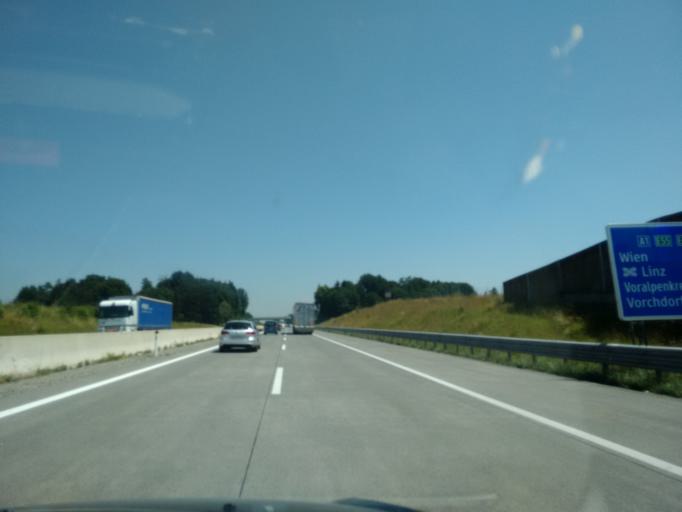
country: AT
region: Upper Austria
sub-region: Politischer Bezirk Gmunden
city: Vorchdorf
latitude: 48.0033
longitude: 13.8737
